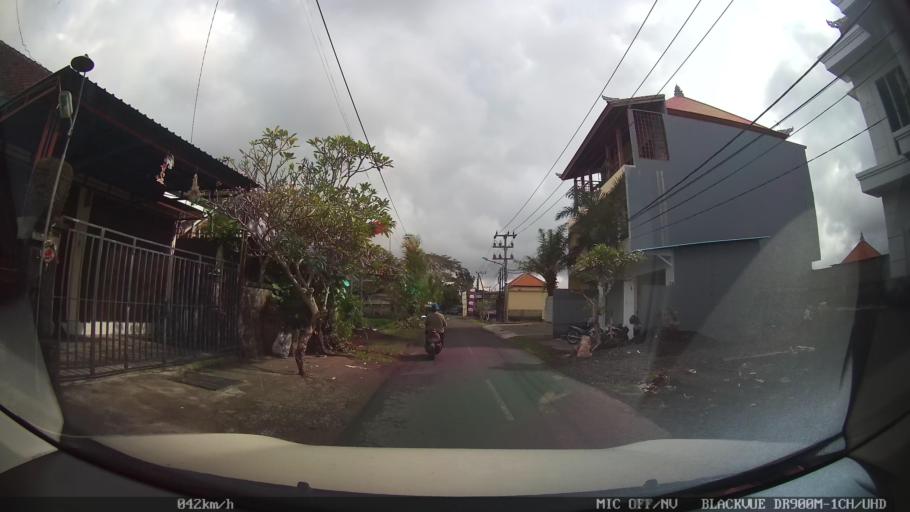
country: ID
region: Bali
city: Banjar Bucu
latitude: -8.5931
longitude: 115.2063
